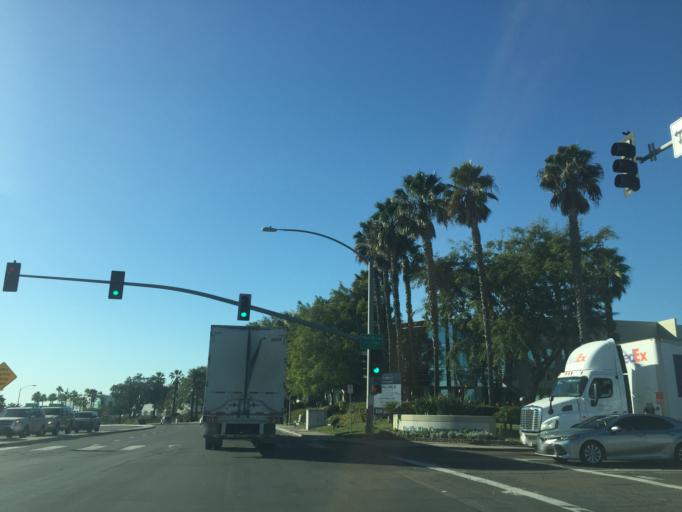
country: MX
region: Baja California
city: Tijuana
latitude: 32.5570
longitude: -116.9358
